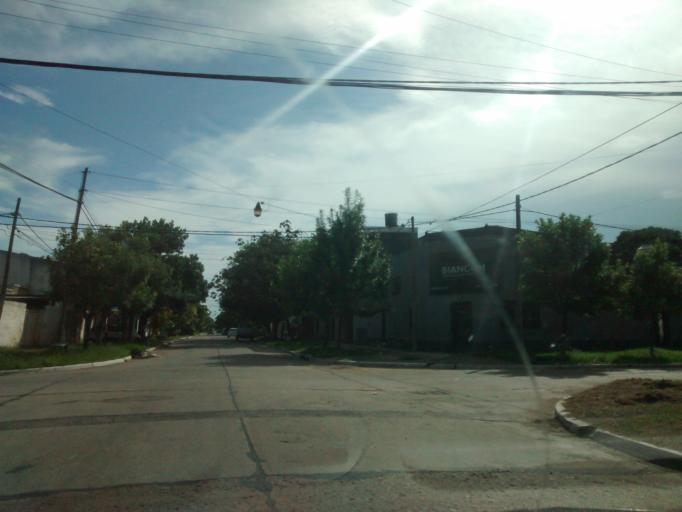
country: AR
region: Chaco
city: Resistencia
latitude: -27.4416
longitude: -58.9918
